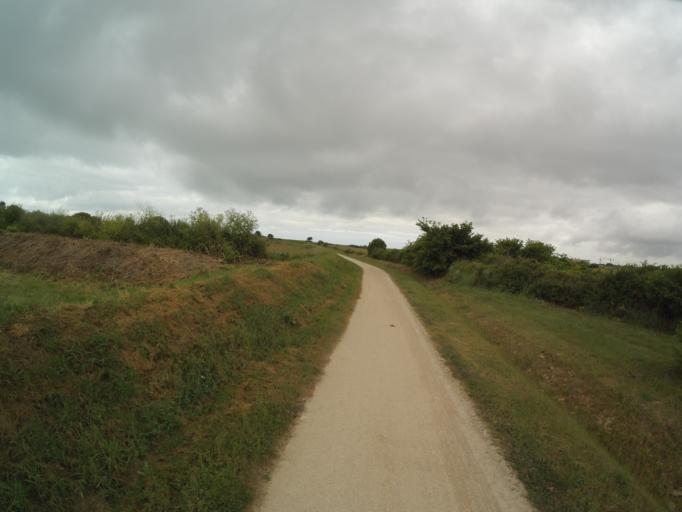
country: FR
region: Poitou-Charentes
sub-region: Departement de la Charente-Maritime
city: Aytre
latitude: 46.1315
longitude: -1.1412
